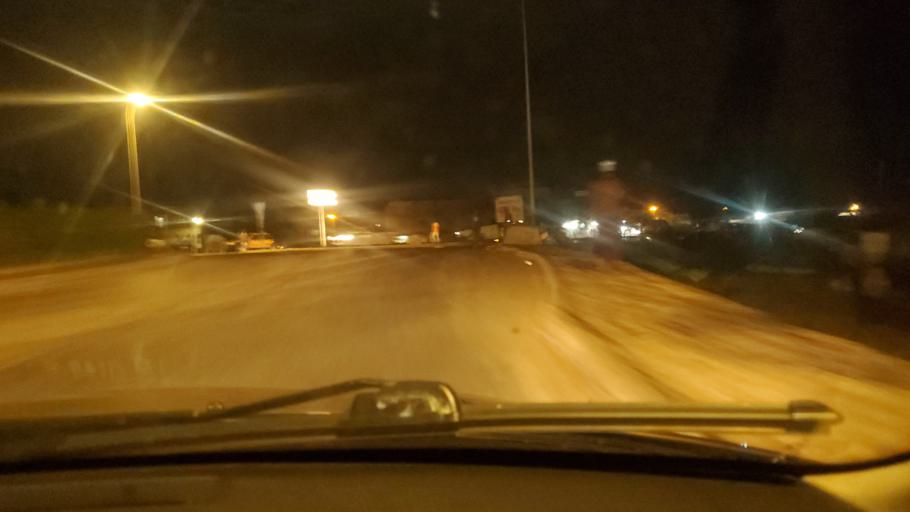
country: SN
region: Dakar
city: Pikine
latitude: 14.7482
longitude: -17.3774
